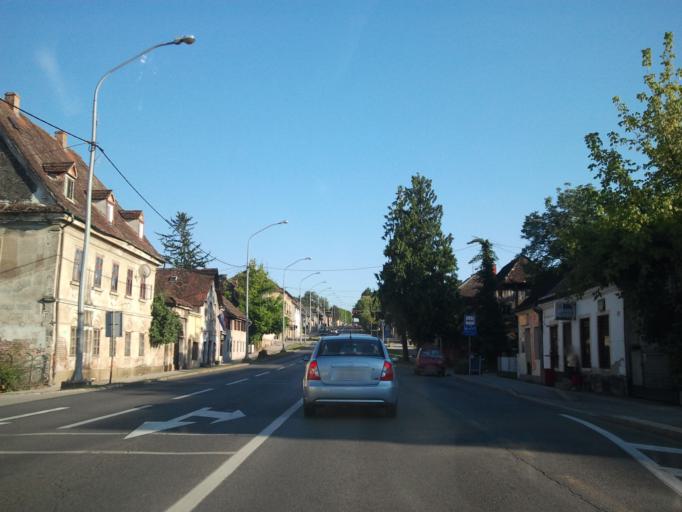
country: HR
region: Sisacko-Moslavacka
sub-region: Grad Sisak
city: Sisak
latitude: 45.4805
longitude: 16.3673
